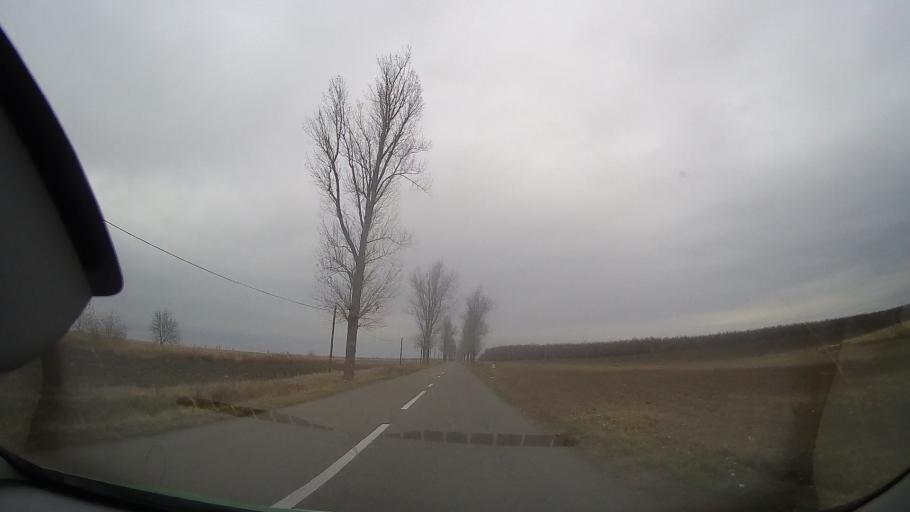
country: RO
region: Braila
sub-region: Comuna Rosiori
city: Rosiori
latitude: 44.8185
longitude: 27.3952
